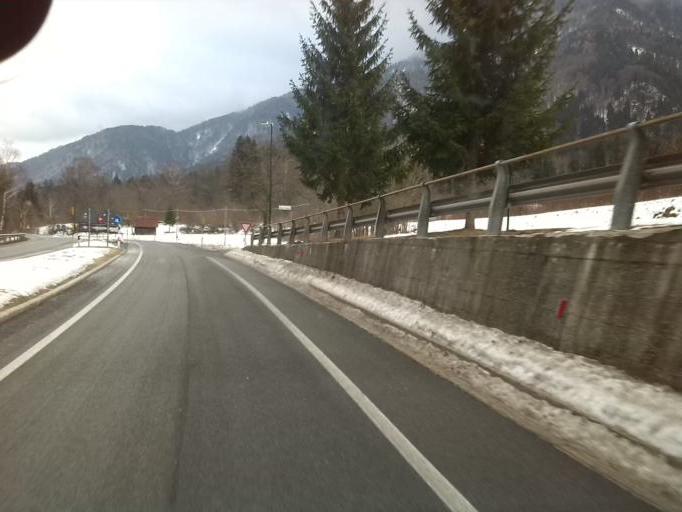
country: IT
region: Friuli Venezia Giulia
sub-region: Provincia di Udine
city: Malborghetto
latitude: 46.5019
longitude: 13.3836
